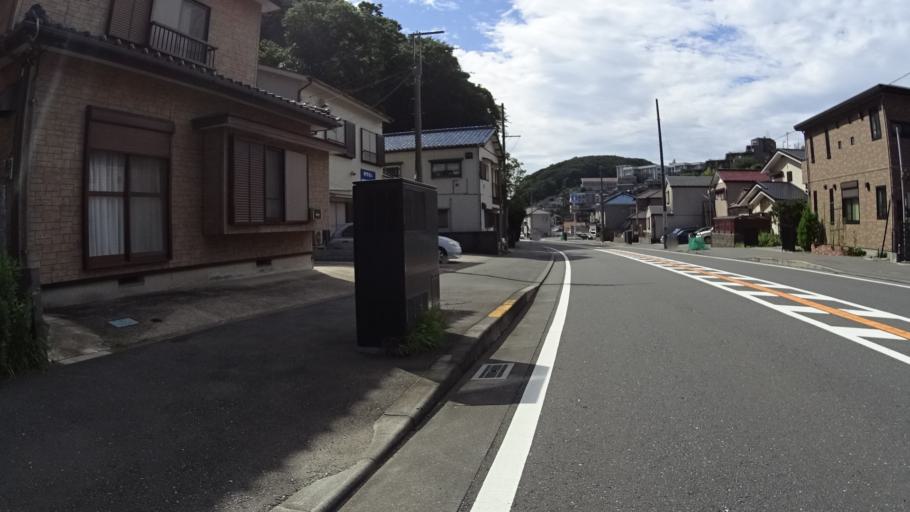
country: JP
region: Kanagawa
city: Yokosuka
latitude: 35.2540
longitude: 139.7100
